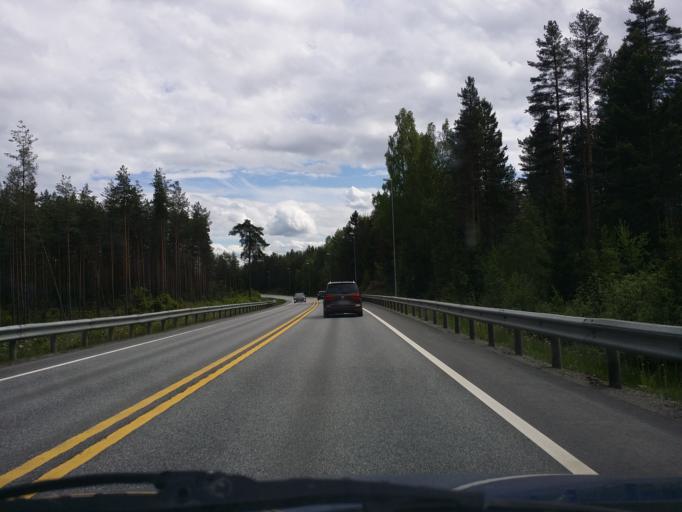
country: NO
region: Hedmark
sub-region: Stange
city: Stange
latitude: 60.7116
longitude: 11.2515
